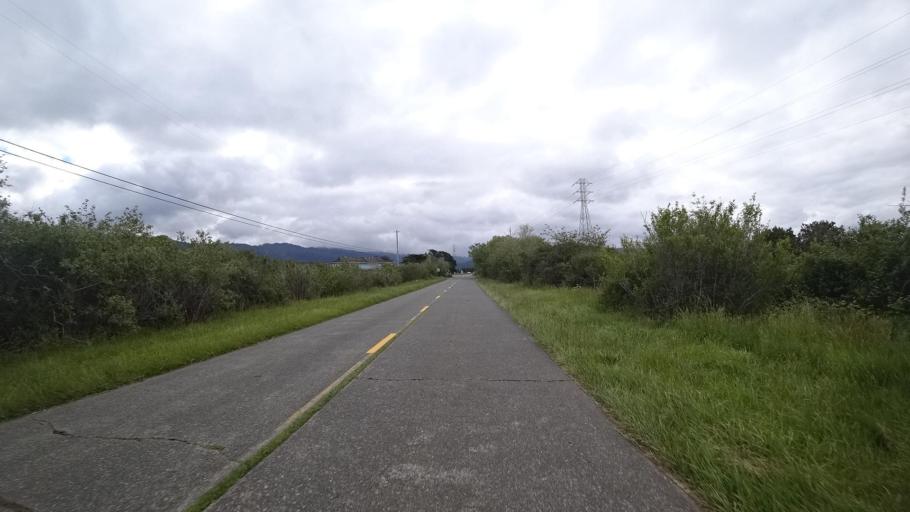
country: US
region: California
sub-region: Humboldt County
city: Arcata
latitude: 40.8530
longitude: -124.0853
